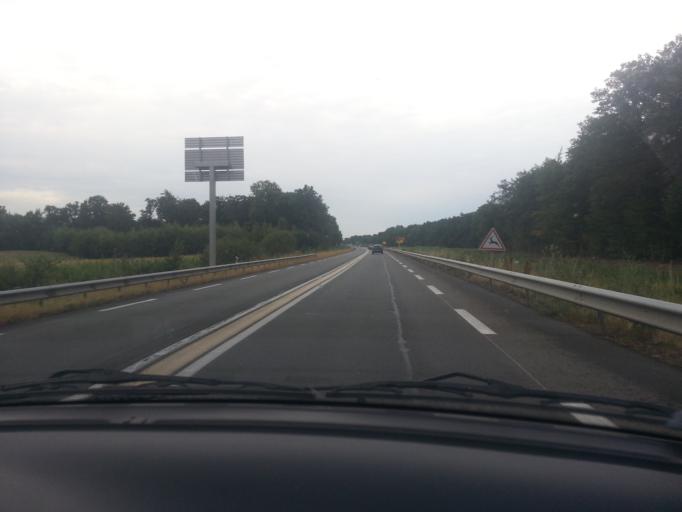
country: FR
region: Bourgogne
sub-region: Departement de Saone-et-Loire
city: Paray-le-Monial
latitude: 46.4837
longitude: 4.1490
